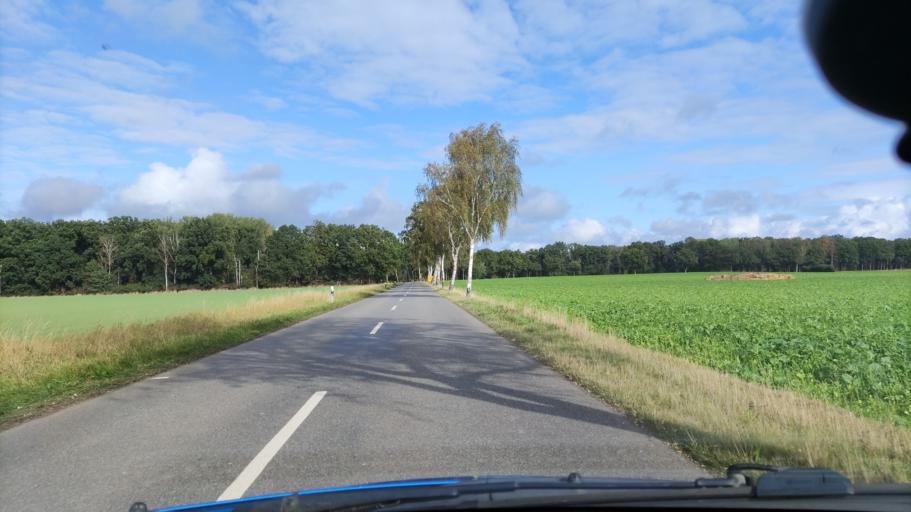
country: DE
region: Lower Saxony
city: Romstedt
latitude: 53.0896
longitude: 10.6749
